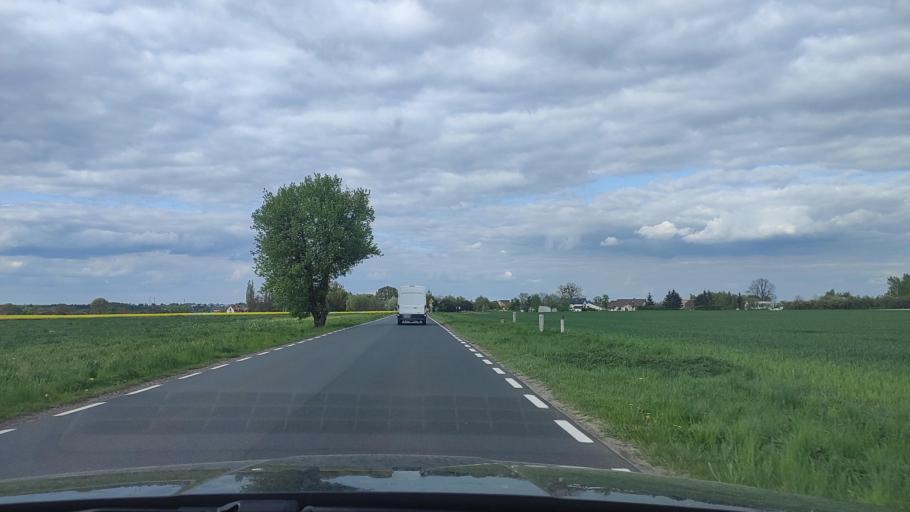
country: PL
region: Greater Poland Voivodeship
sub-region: Powiat poznanski
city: Kostrzyn
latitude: 52.4403
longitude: 17.1676
